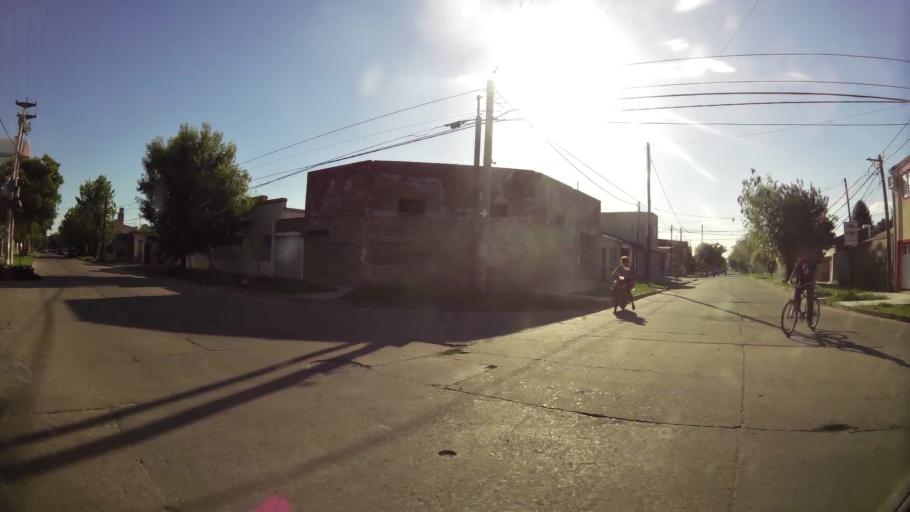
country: AR
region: Santa Fe
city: Santa Fe de la Vera Cruz
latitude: -31.6095
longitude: -60.6984
